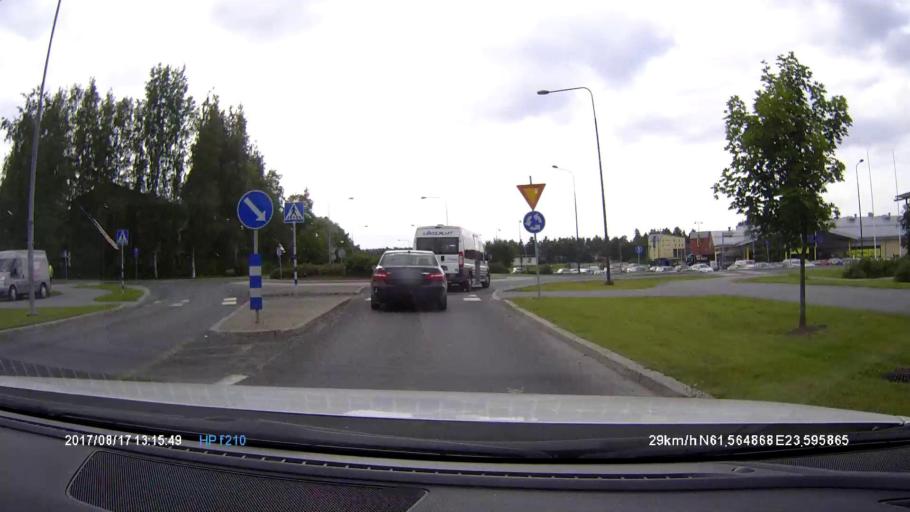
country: FI
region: Pirkanmaa
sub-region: Tampere
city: Yloejaervi
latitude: 61.5649
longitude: 23.5959
